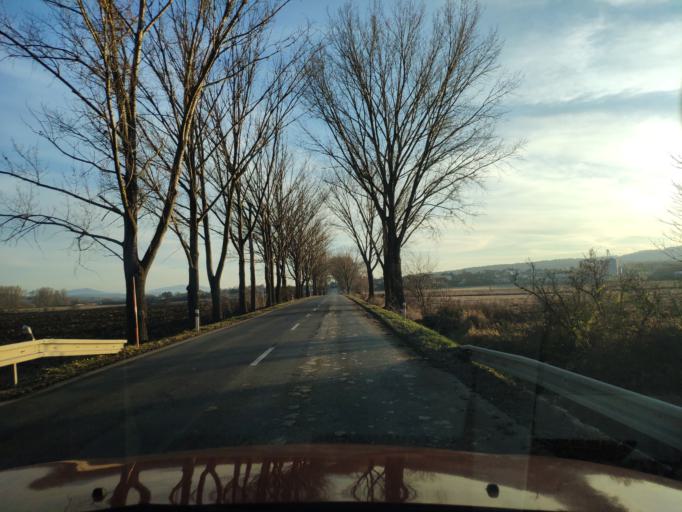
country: SK
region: Kosicky
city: Kosice
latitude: 48.8104
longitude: 21.3007
